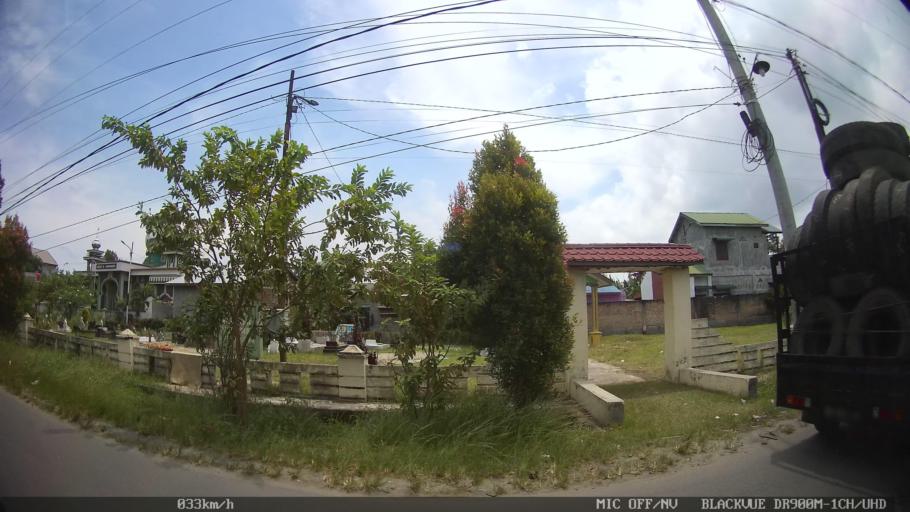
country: ID
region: North Sumatra
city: Labuhan Deli
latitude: 3.7087
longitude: 98.6763
